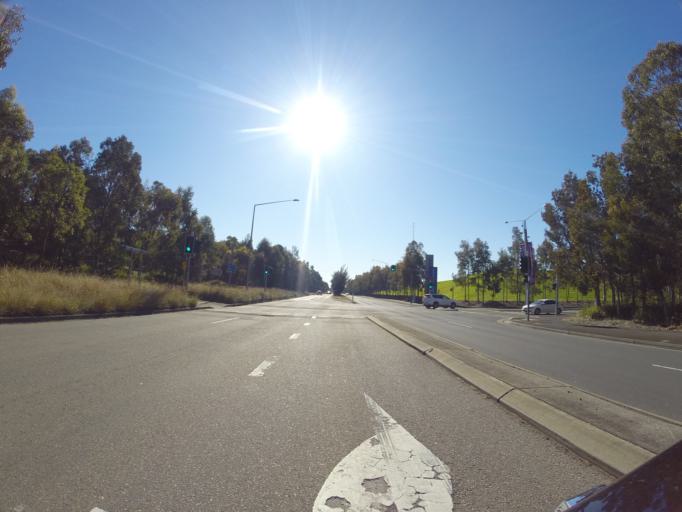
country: AU
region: New South Wales
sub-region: Auburn
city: Auburn
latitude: -33.8422
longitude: 151.0585
